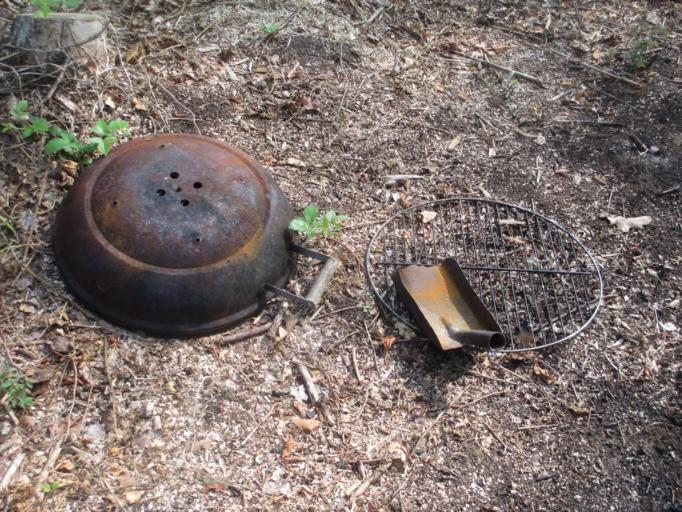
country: FR
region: Picardie
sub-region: Departement de l'Oise
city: Dreslincourt
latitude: 49.5735
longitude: 2.8989
